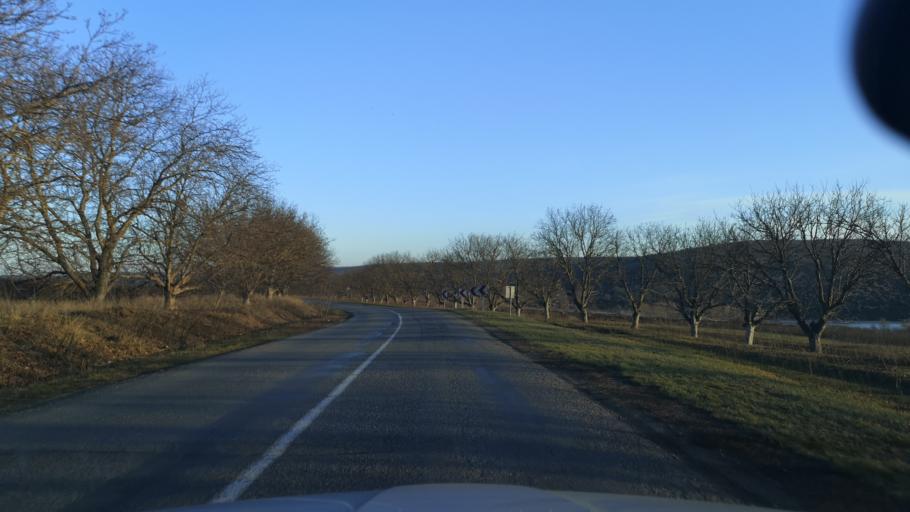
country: MD
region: Orhei
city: Orhei
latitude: 47.2857
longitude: 28.8257
